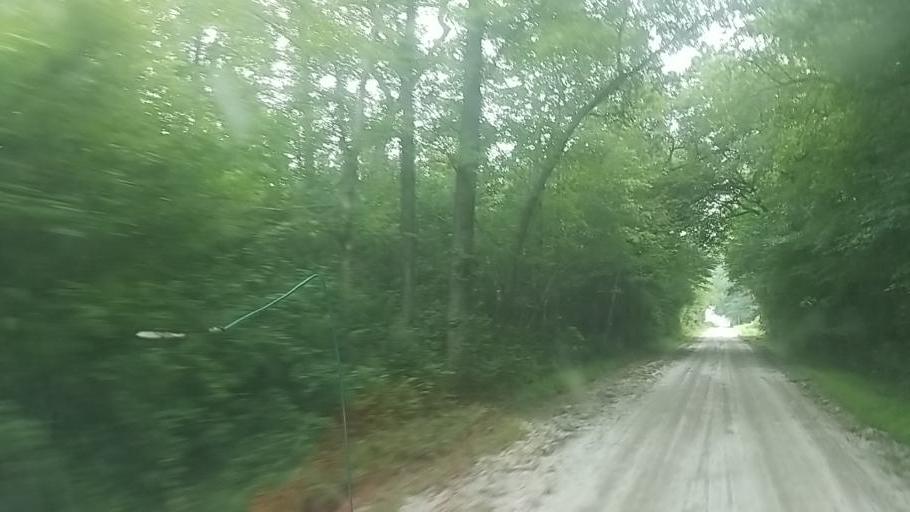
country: US
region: Maryland
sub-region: Wicomico County
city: Pittsville
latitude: 38.4444
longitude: -75.4386
